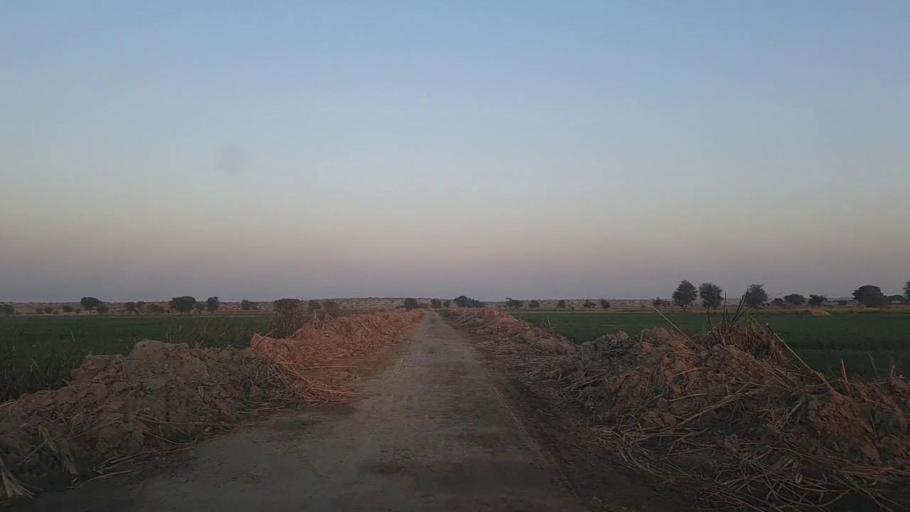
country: PK
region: Sindh
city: Jam Sahib
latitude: 26.3876
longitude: 68.6961
